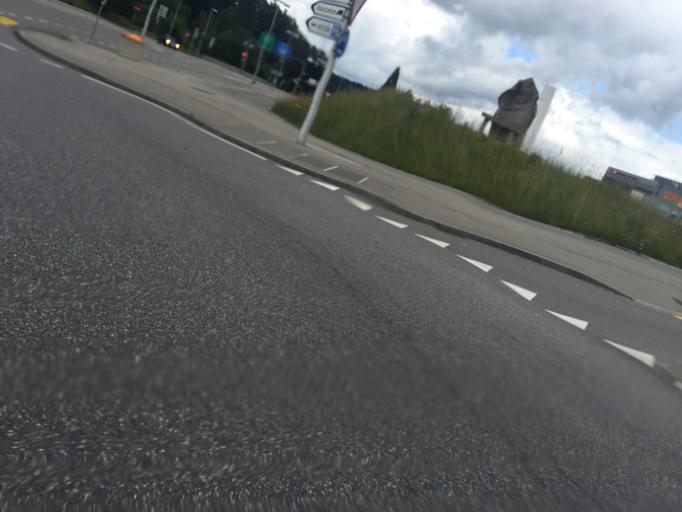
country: CH
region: Bern
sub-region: Bern-Mittelland District
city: Wohlen
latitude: 46.9430
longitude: 7.3701
